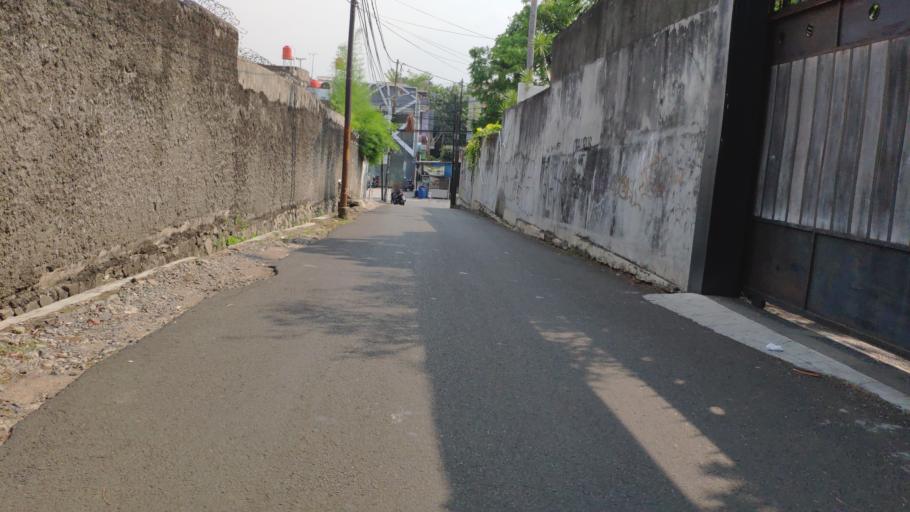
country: ID
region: Jakarta Raya
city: Jakarta
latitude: -6.2734
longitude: 106.8194
